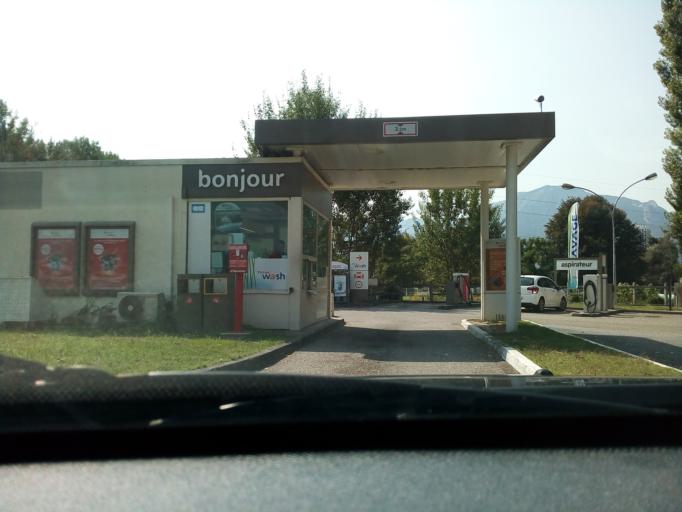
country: FR
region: Rhone-Alpes
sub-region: Departement de l'Isere
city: La Tronche
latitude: 45.1953
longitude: 5.7499
